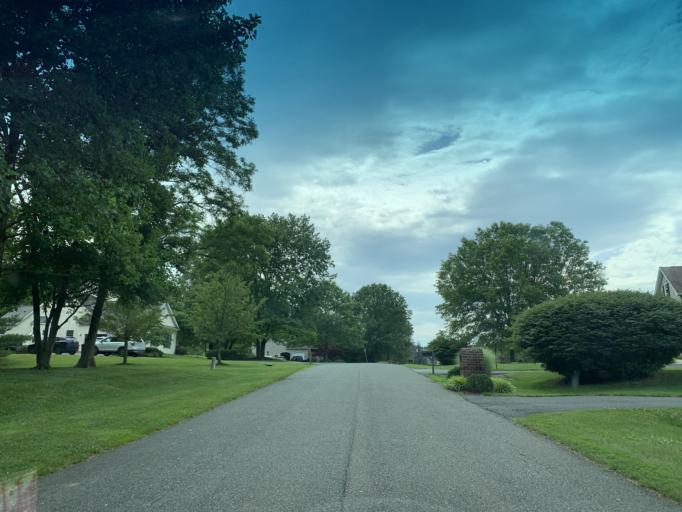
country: US
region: Maryland
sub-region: Harford County
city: Fallston
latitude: 39.5248
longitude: -76.4071
